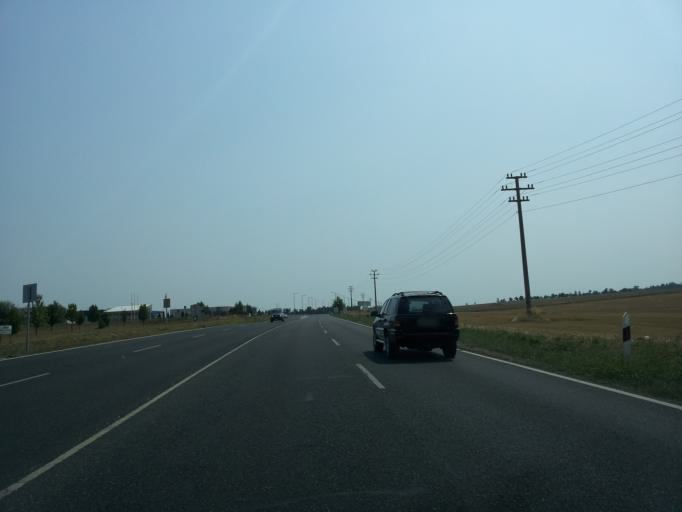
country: HU
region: Veszprem
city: Veszprem
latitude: 47.0760
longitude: 17.9167
